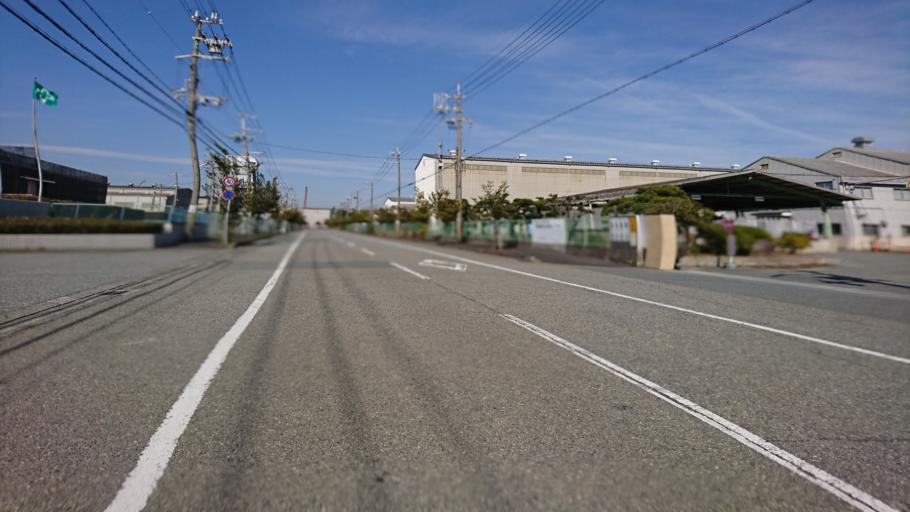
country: JP
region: Hyogo
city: Kakogawacho-honmachi
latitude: 34.6995
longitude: 134.8489
